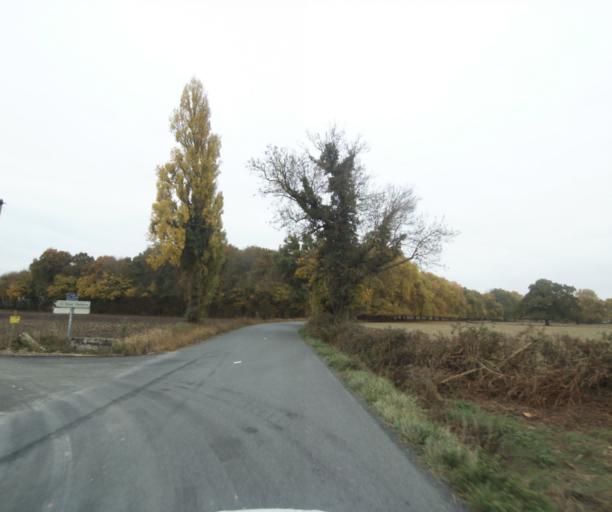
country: FR
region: Poitou-Charentes
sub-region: Departement de la Charente-Maritime
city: Chermignac
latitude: 45.7188
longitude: -0.6749
